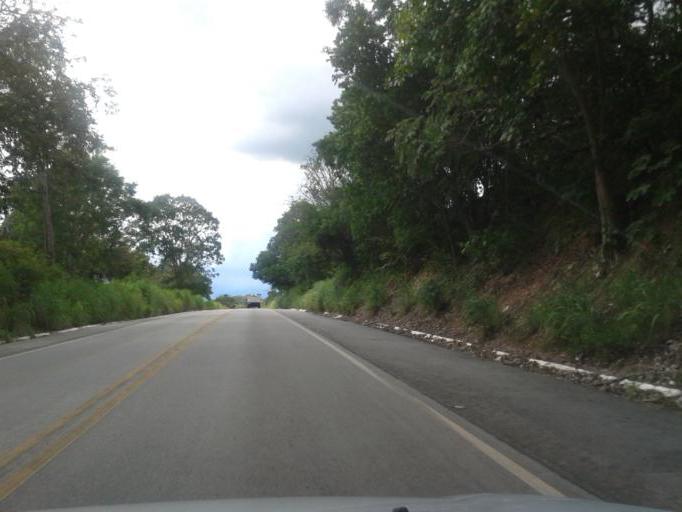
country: BR
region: Goias
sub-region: Goias
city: Goias
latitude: -15.8581
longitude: -50.0904
